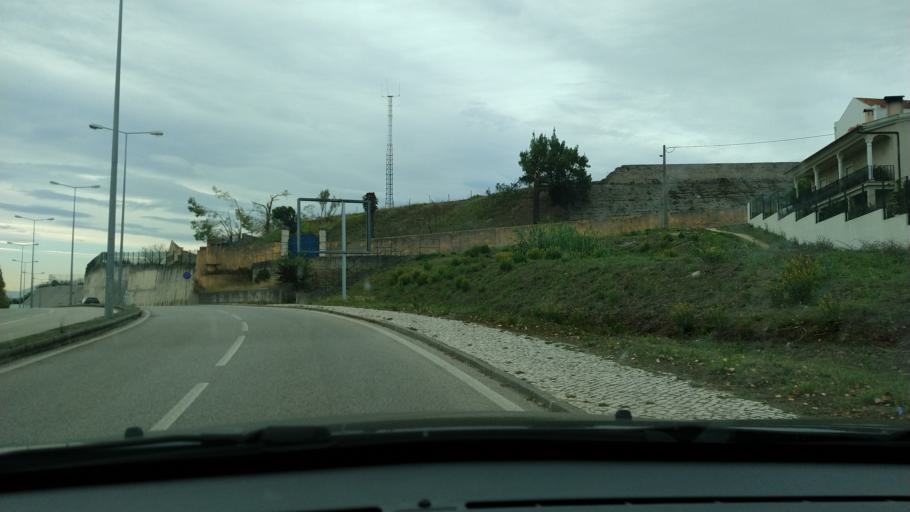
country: PT
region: Coimbra
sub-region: Figueira da Foz
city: Figueira da Foz
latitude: 40.1557
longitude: -8.8501
